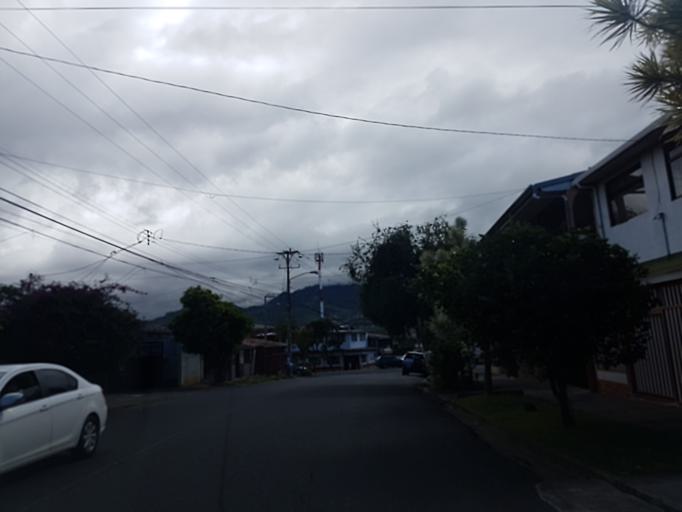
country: CR
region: San Jose
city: San Felipe
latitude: 9.9213
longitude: -84.0995
